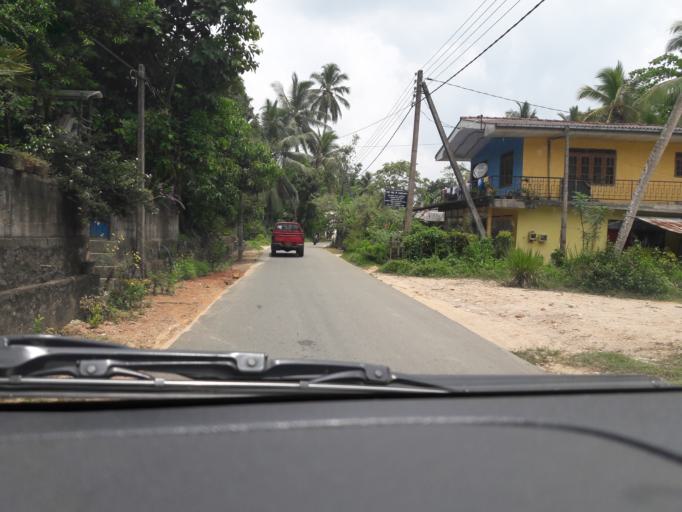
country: LK
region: Southern
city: Galle
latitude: 6.1736
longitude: 80.2865
